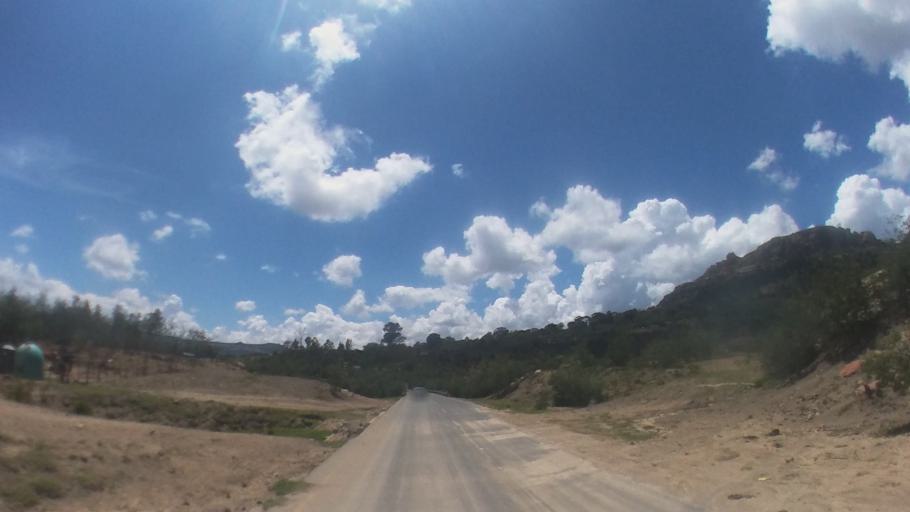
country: LS
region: Maseru
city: Nako
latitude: -29.6163
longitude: 27.5571
